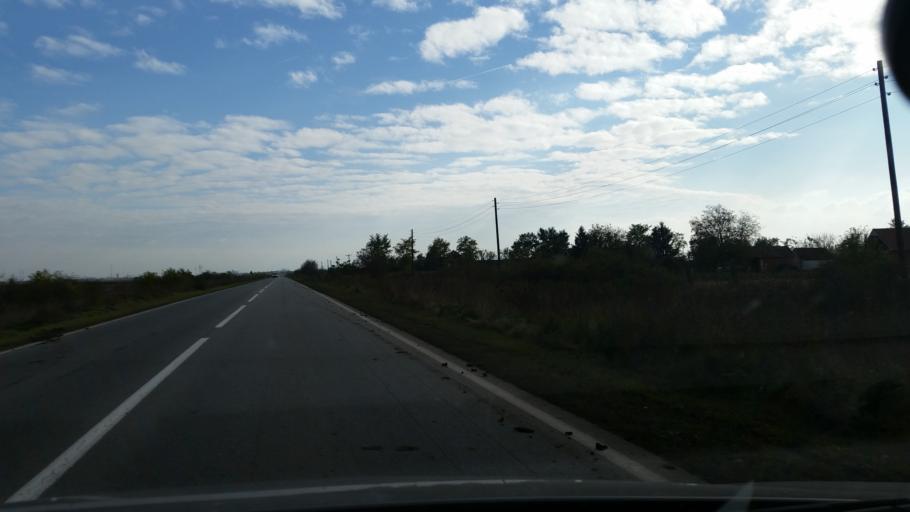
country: RS
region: Autonomna Pokrajina Vojvodina
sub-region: Srednjebanatski Okrug
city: Zrenjanin
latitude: 45.4258
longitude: 20.3704
